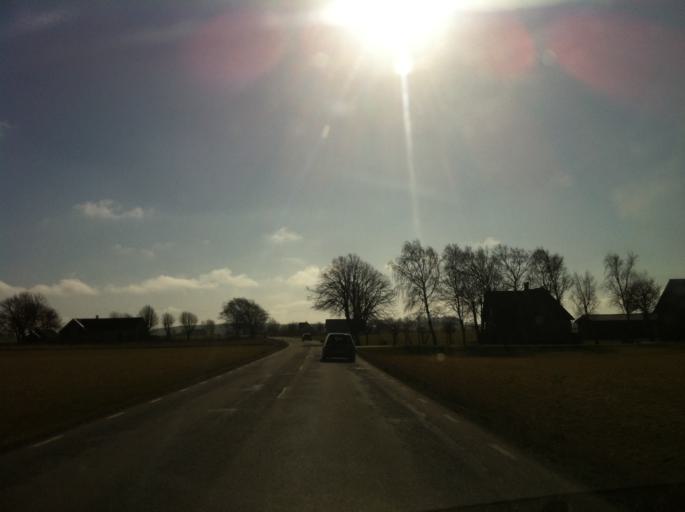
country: SE
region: Skane
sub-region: Bastads Kommun
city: Forslov
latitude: 56.3170
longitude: 12.8384
